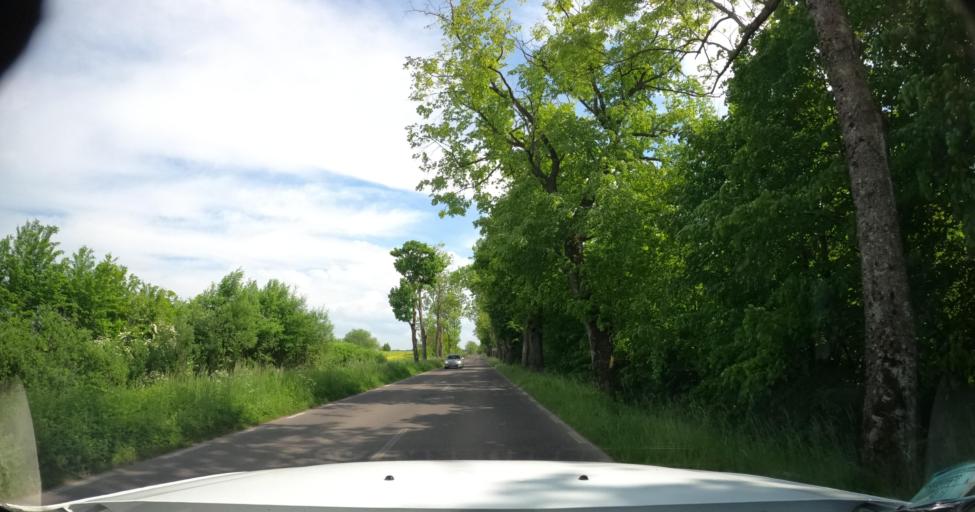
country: PL
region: Warmian-Masurian Voivodeship
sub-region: Powiat lidzbarski
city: Lidzbark Warminski
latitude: 54.1435
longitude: 20.5639
